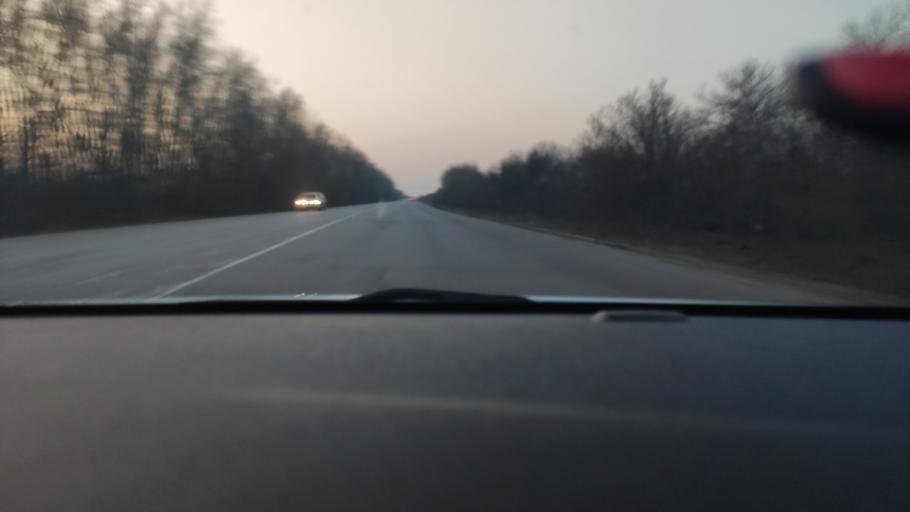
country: RU
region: Voronezj
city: Kolodeznyy
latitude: 51.2739
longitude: 39.0469
